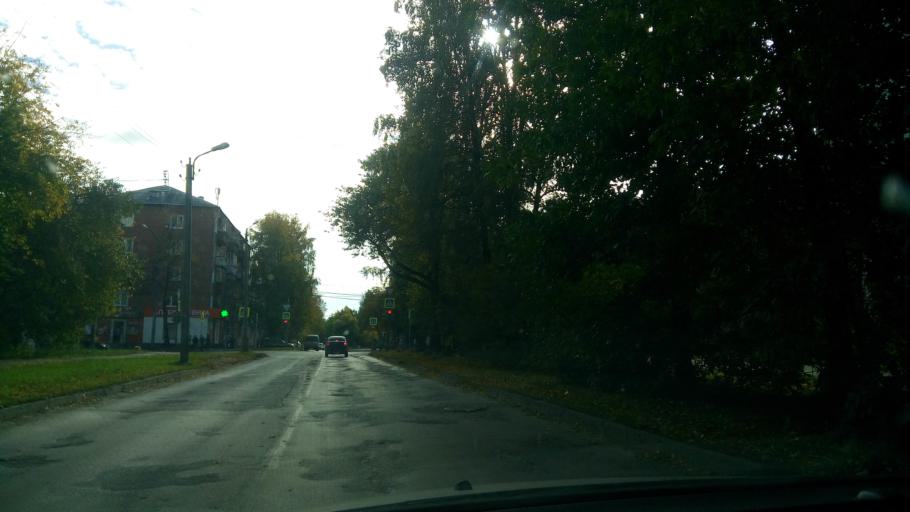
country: RU
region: Sverdlovsk
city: Yekaterinburg
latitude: 56.9034
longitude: 60.6038
